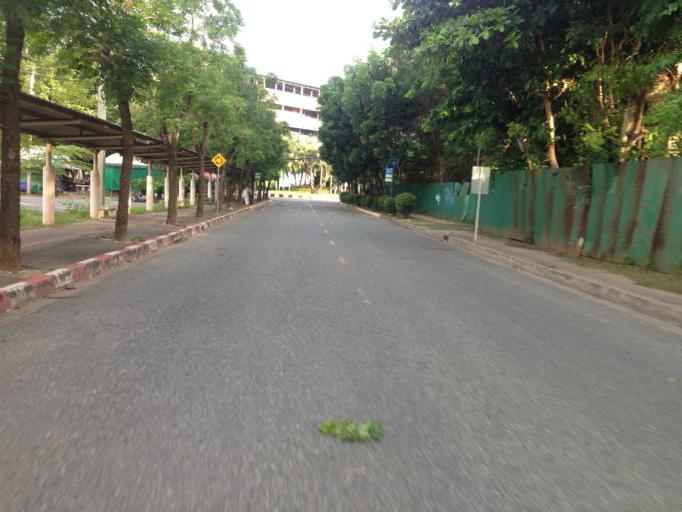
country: TH
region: Chon Buri
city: Chon Buri
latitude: 13.2783
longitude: 100.9255
